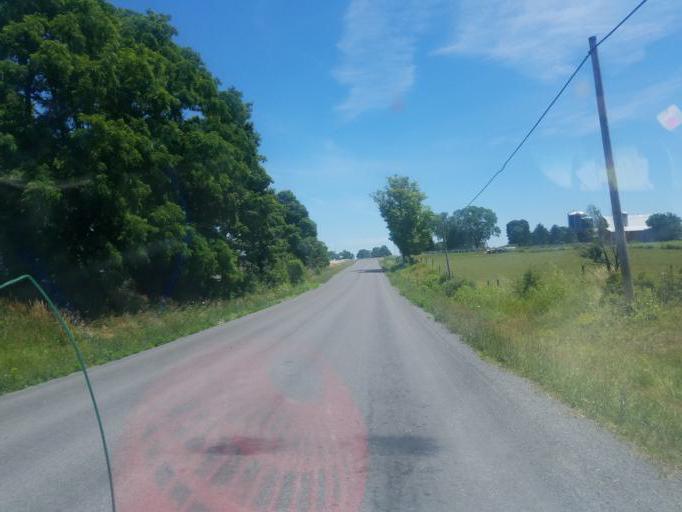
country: US
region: New York
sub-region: Yates County
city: Penn Yan
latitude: 42.6523
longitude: -77.0248
